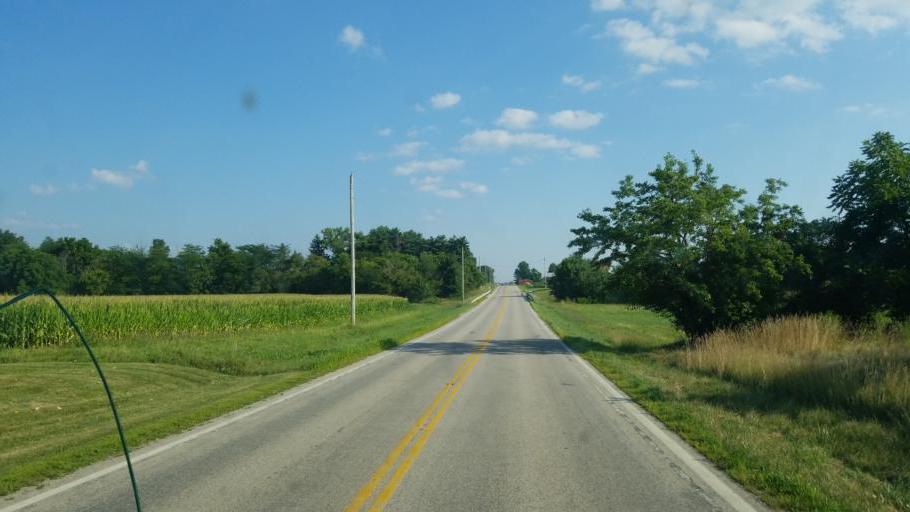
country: US
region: Ohio
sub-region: Crawford County
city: Bucyrus
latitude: 40.8867
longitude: -83.0112
